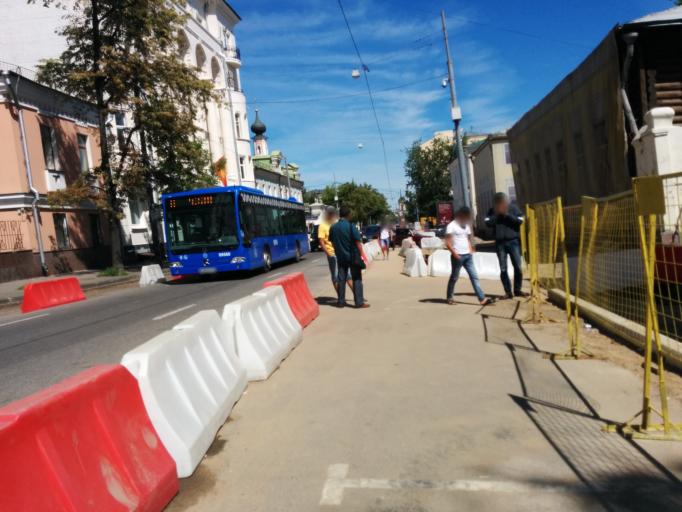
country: RU
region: Moscow
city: Zamoskvorech'ye
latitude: 55.7318
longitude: 37.6243
